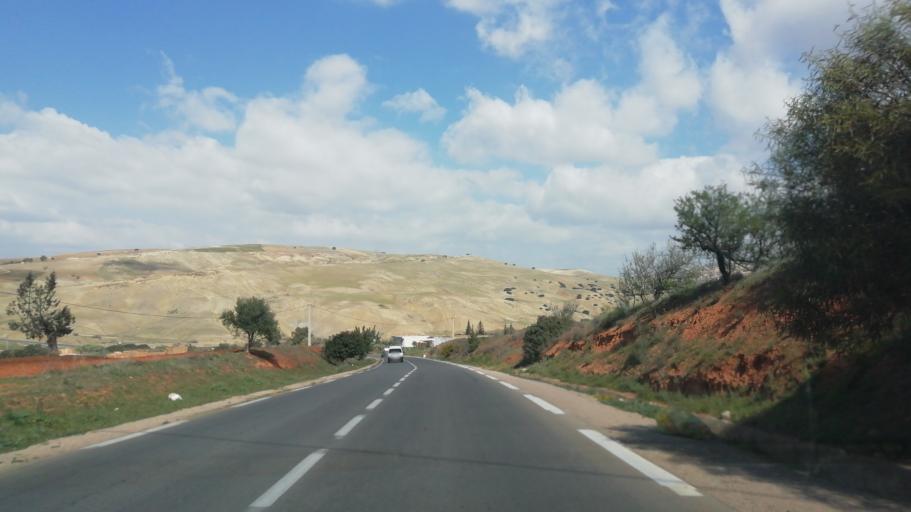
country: DZ
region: Mascara
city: Mascara
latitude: 35.5362
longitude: 0.1127
